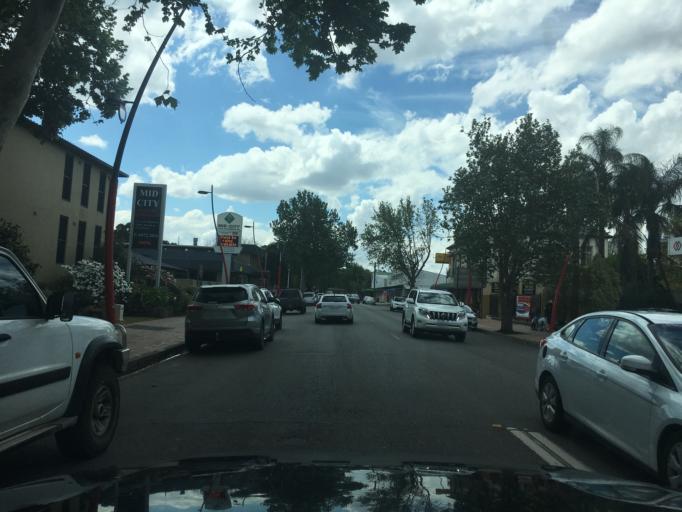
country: AU
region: New South Wales
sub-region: Singleton
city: Singleton
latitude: -32.5629
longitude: 151.1694
